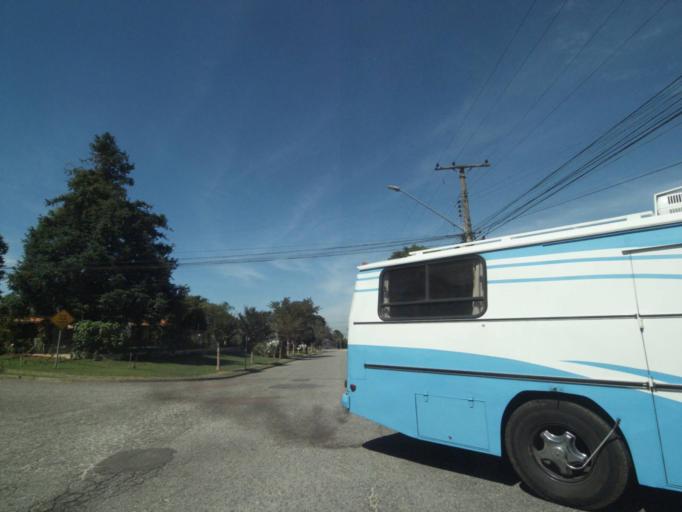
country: BR
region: Parana
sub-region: Curitiba
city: Curitiba
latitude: -25.4581
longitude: -49.2456
